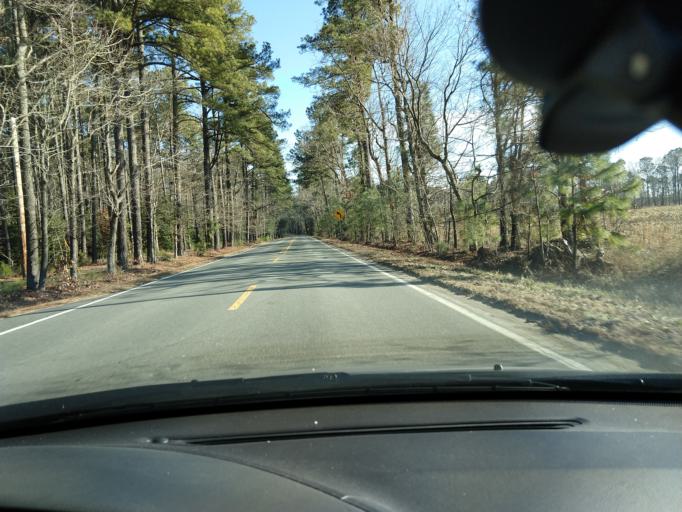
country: US
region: Virginia
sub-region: Surry County
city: Surry
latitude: 37.2653
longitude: -76.8939
